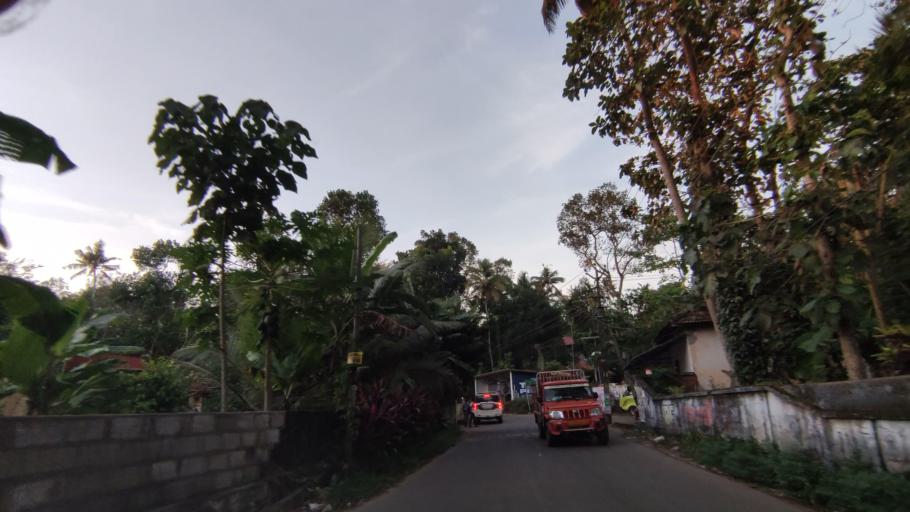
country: IN
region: Kerala
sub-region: Kottayam
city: Kottayam
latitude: 9.6480
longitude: 76.5099
